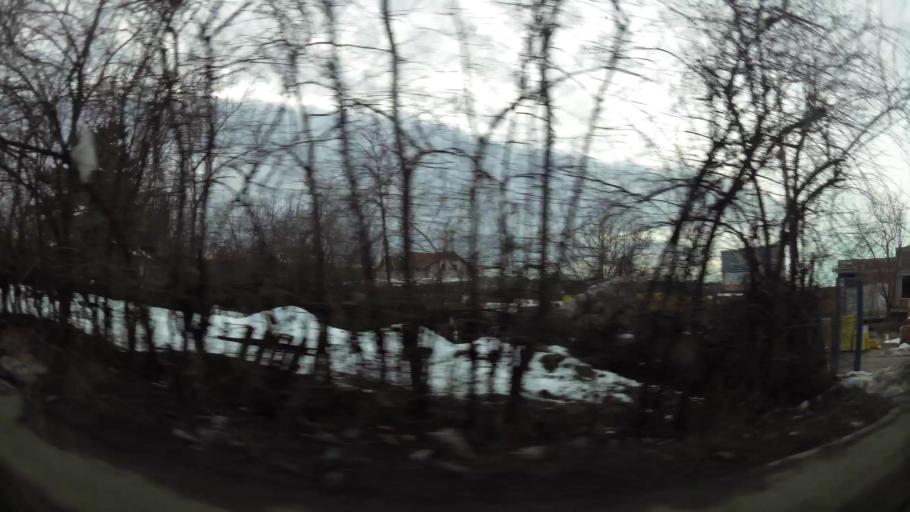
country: RS
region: Central Serbia
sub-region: Belgrade
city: Vozdovac
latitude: 44.7472
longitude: 20.4769
